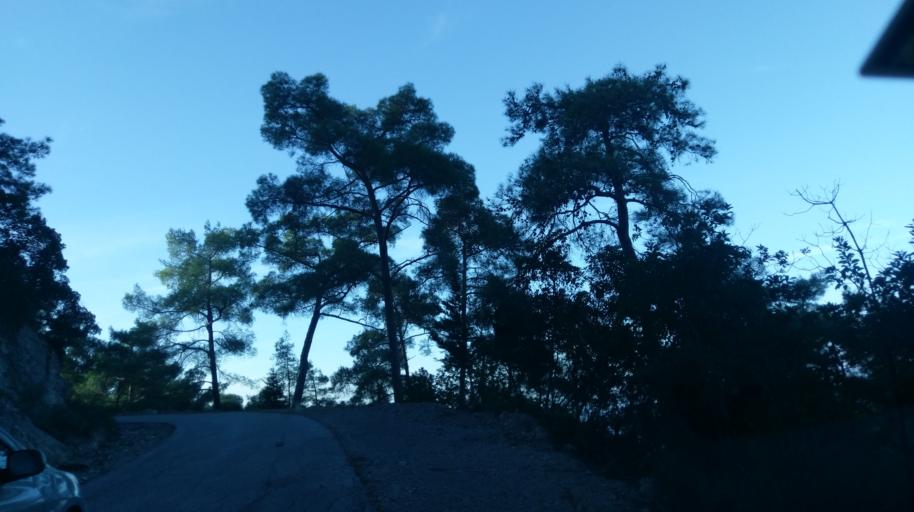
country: CY
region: Ammochostos
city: Lefkonoiko
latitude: 35.3119
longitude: 33.5805
